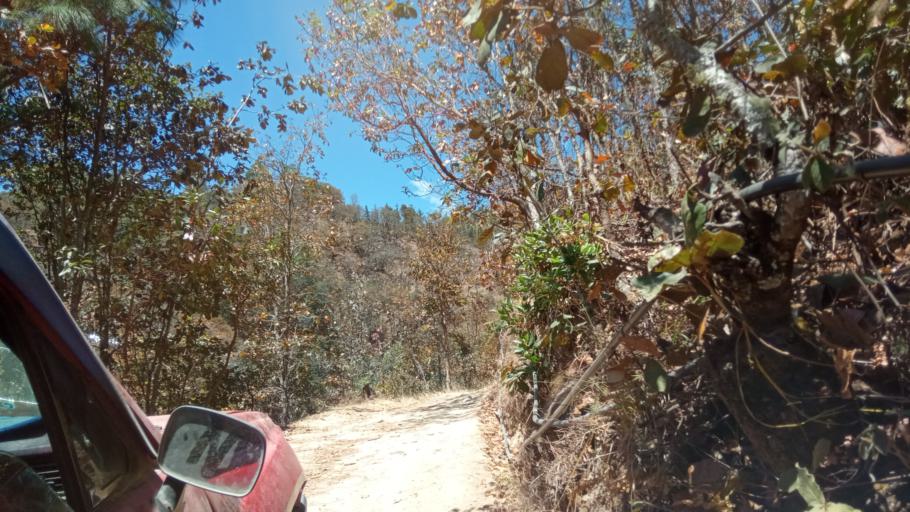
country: GT
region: San Marcos
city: Tejutla
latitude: 15.1364
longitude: -91.7909
